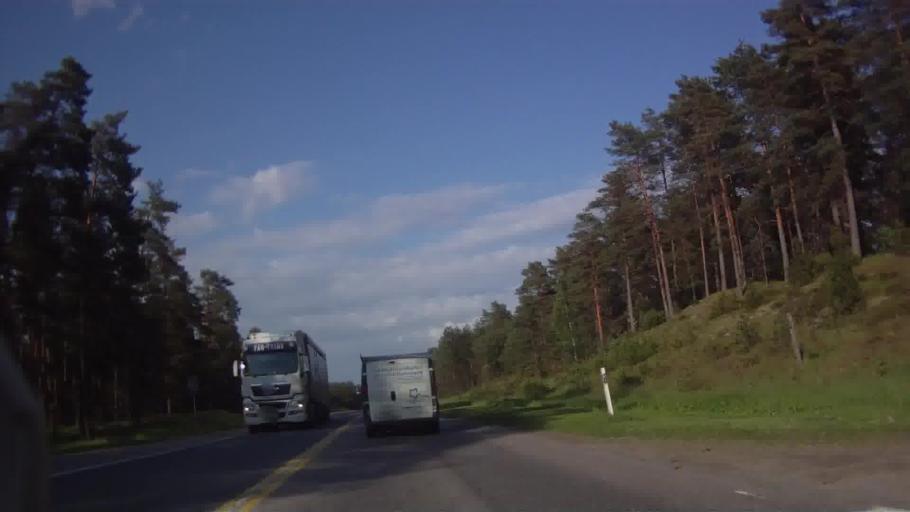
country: LV
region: Garkalne
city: Garkalne
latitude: 57.0648
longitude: 24.4726
